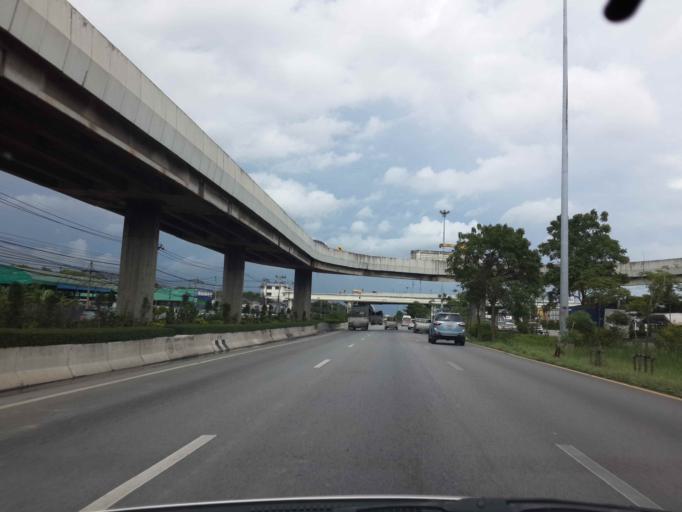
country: TH
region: Bangkok
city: Bang Bon
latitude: 13.6135
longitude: 100.3809
